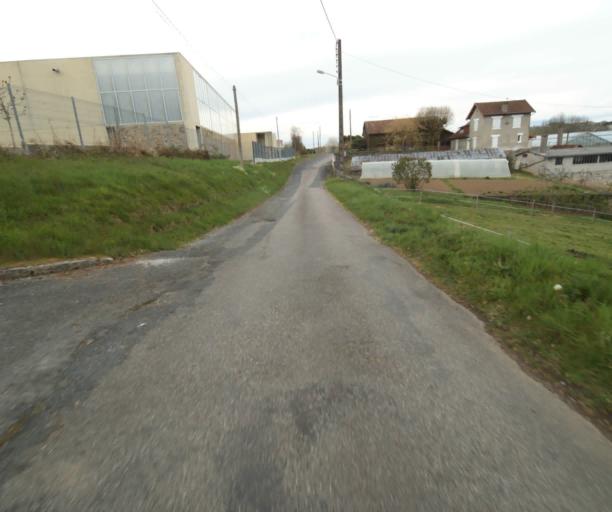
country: FR
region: Limousin
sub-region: Departement de la Correze
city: Tulle
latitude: 45.2558
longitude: 1.7693
